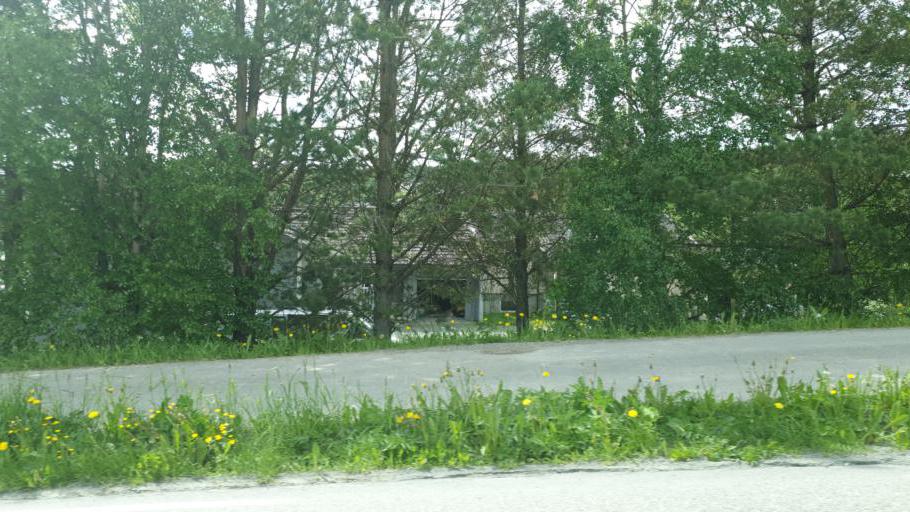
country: NO
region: Nord-Trondelag
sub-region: Leksvik
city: Leksvik
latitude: 63.6709
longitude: 10.6100
